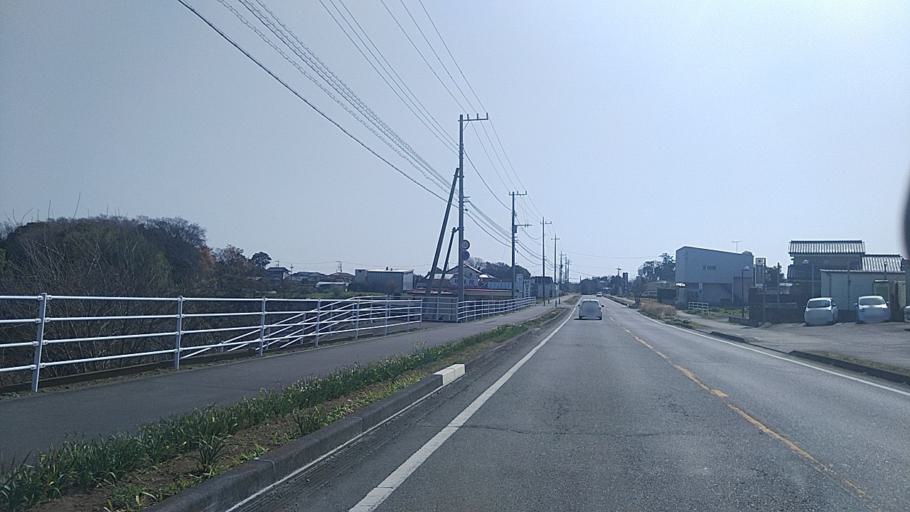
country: JP
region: Ibaraki
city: Toride
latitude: 35.8873
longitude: 140.1038
